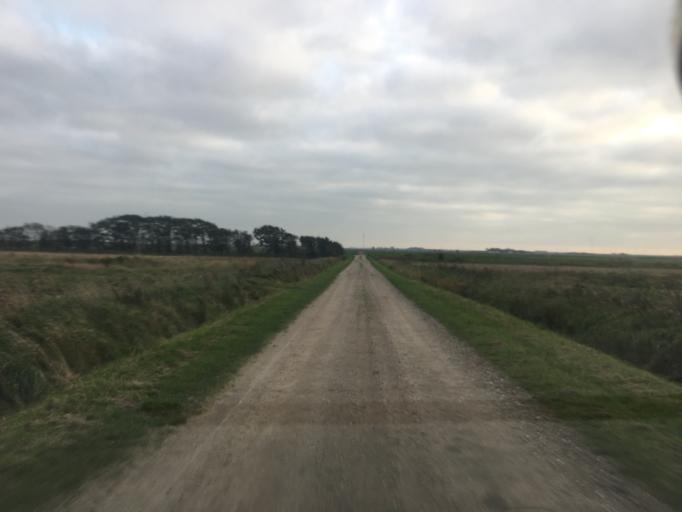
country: DE
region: Schleswig-Holstein
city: Rodenas
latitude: 54.9605
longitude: 8.7386
